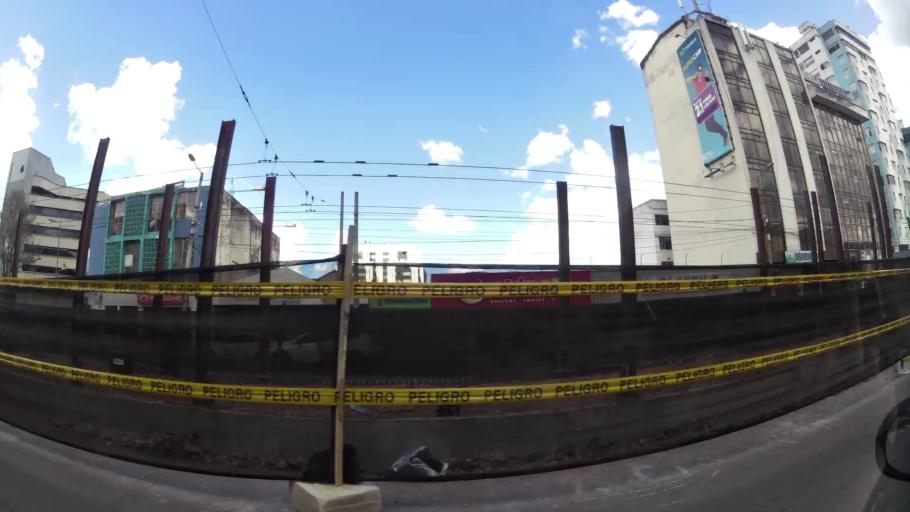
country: EC
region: Pichincha
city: Quito
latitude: -0.1985
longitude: -78.4962
